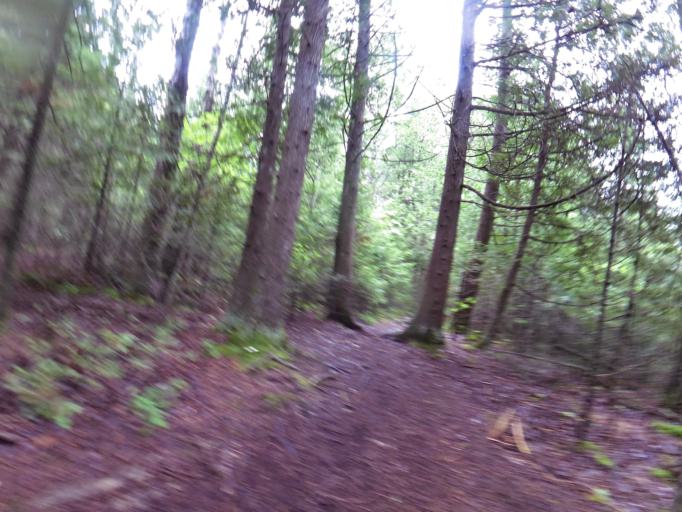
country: CA
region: Ontario
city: Tobermory
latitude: 45.2586
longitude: -81.6468
